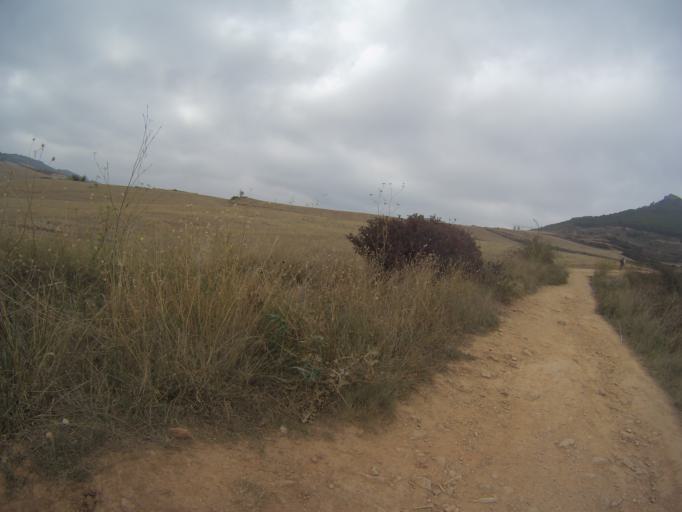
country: ES
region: Navarre
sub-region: Provincia de Navarra
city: Villamayor de Monjardin
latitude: 42.6320
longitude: -2.0962
